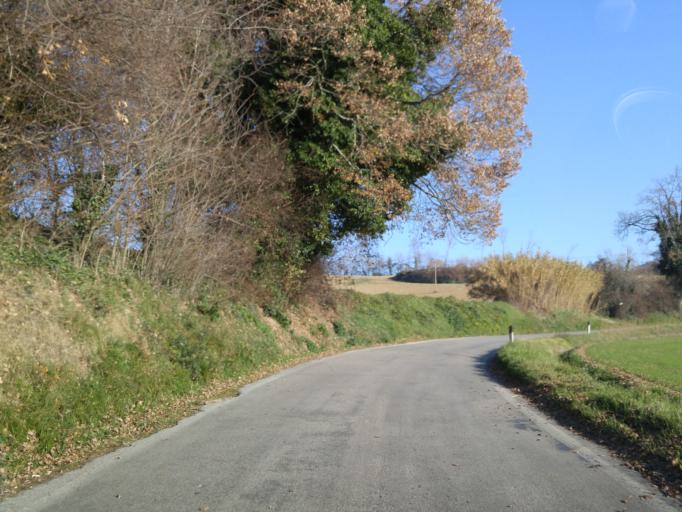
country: IT
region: The Marches
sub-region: Provincia di Pesaro e Urbino
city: Montefelcino
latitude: 43.7258
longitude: 12.8410
